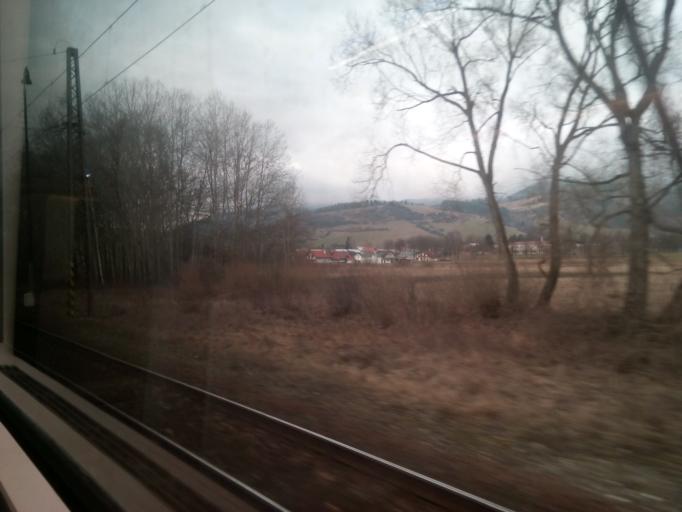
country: SK
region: Zilinsky
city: Ruzomberok
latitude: 49.1001
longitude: 19.4182
